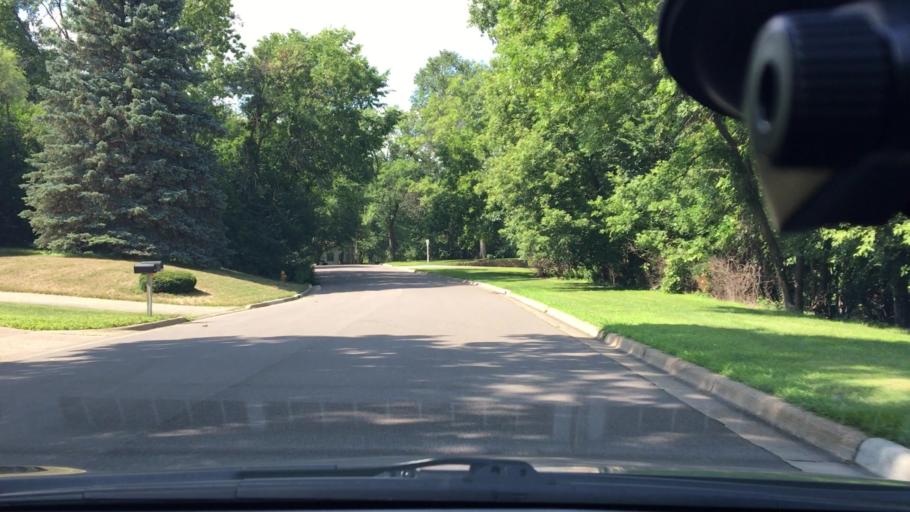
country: US
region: Minnesota
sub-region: Hennepin County
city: Golden Valley
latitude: 44.9960
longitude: -93.3871
